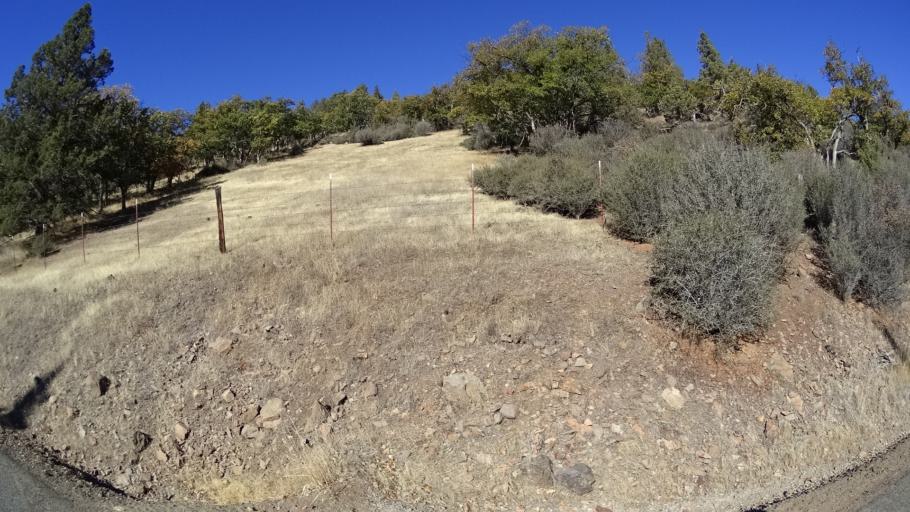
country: US
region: California
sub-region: Siskiyou County
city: Montague
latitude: 41.9635
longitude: -122.3105
